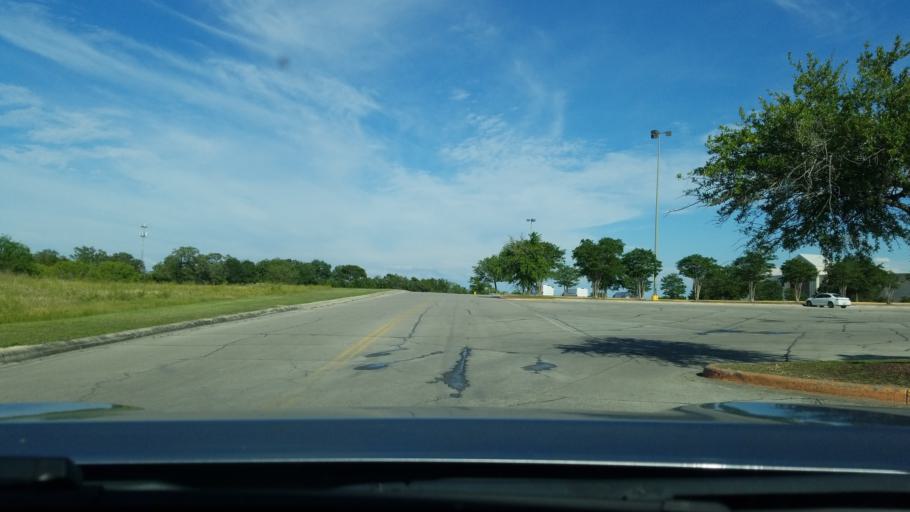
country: US
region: Texas
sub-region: Bexar County
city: Live Oak
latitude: 29.5990
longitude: -98.3503
